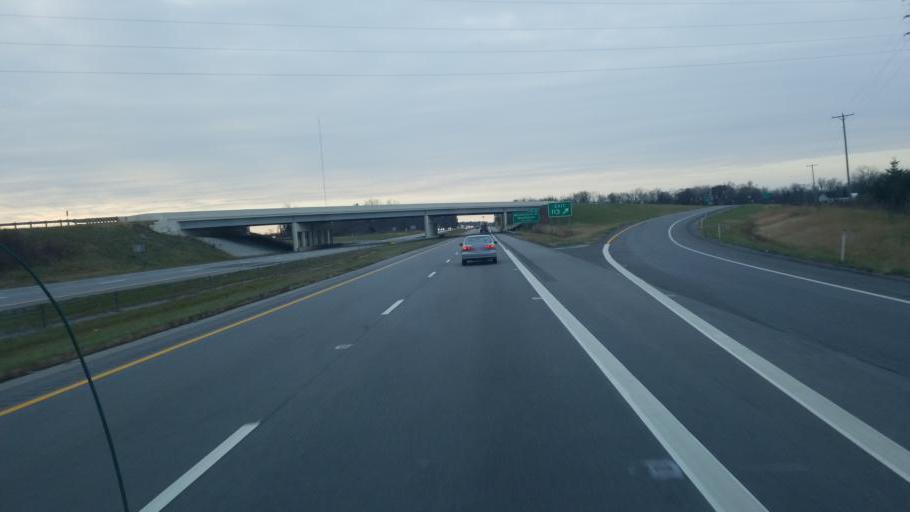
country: US
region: Ohio
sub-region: Auglaize County
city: Wapakoneta
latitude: 40.5872
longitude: -84.1642
